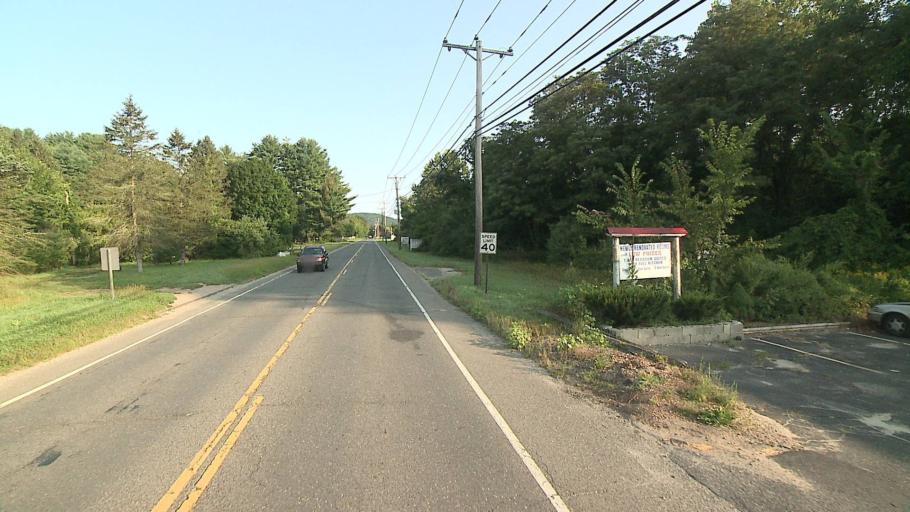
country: US
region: Connecticut
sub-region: Litchfield County
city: New Milford
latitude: 41.5848
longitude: -73.4436
